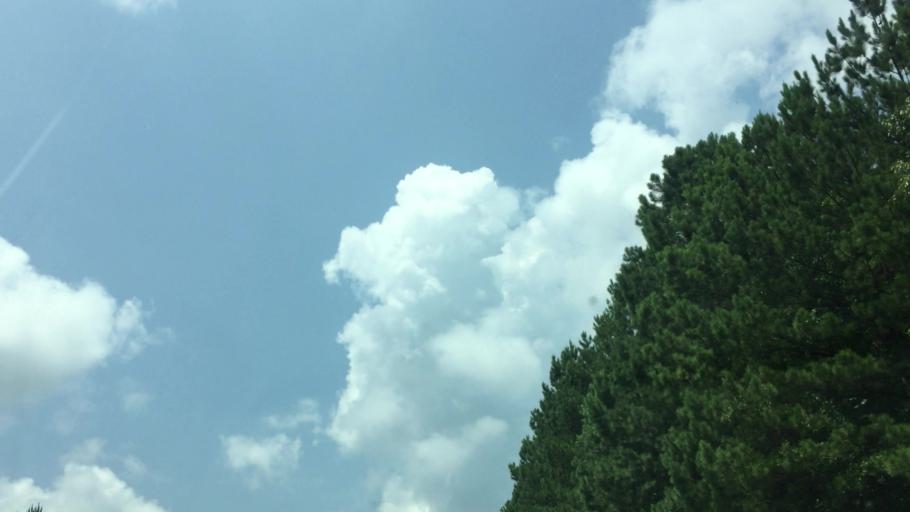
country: US
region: Georgia
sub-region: Fulton County
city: Chattahoochee Hills
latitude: 33.5628
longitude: -84.7744
